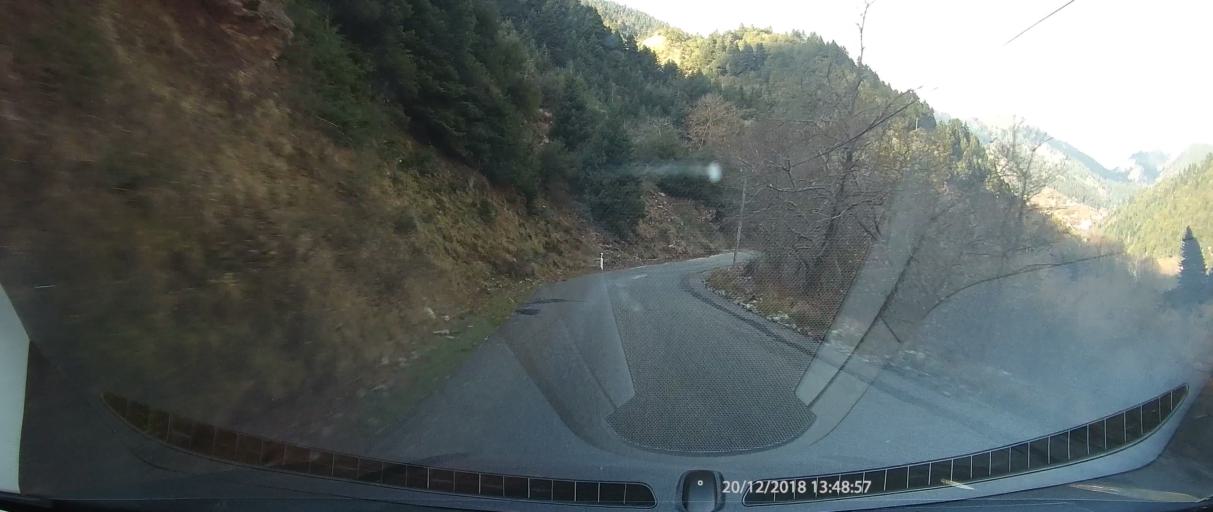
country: GR
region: West Greece
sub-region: Nomos Aitolias kai Akarnanias
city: Paravola
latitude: 38.6891
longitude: 21.6085
